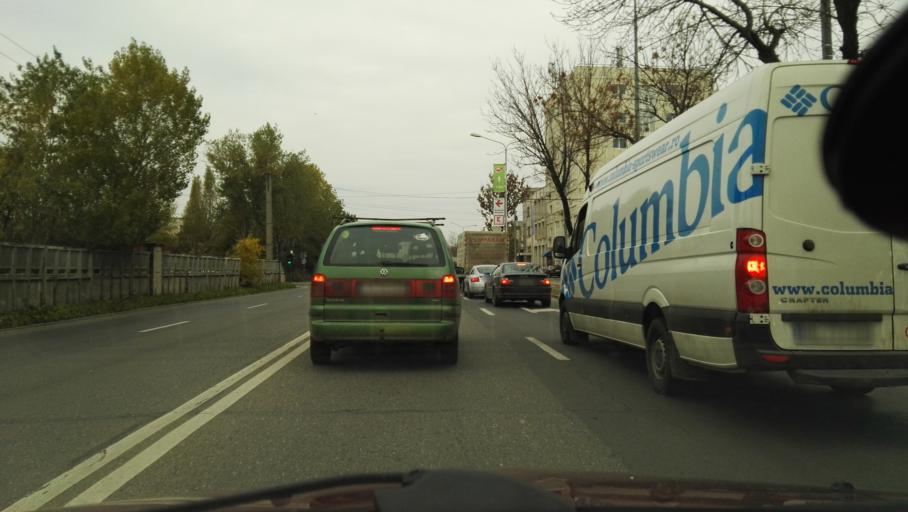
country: RO
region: Bucuresti
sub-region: Municipiul Bucuresti
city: Bucuresti
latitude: 44.4109
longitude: 26.0841
